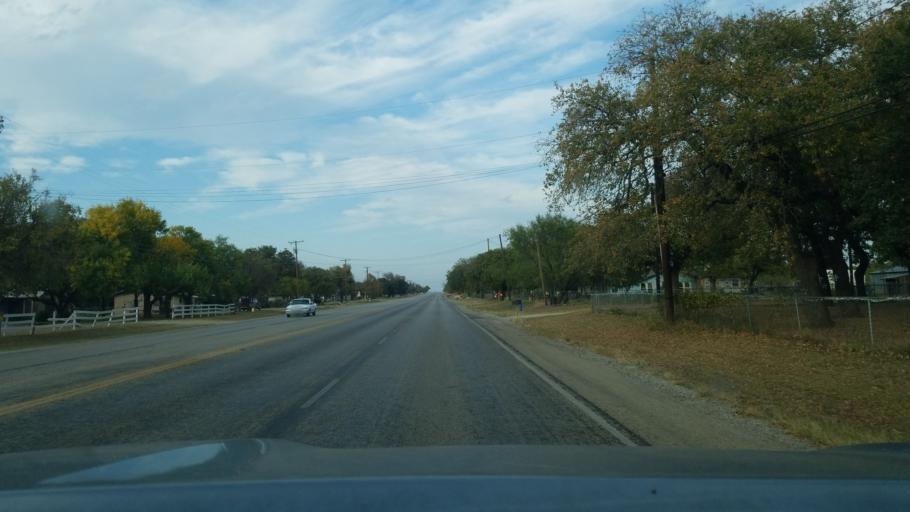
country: US
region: Texas
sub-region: Brown County
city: Early
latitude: 31.7614
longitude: -98.9573
